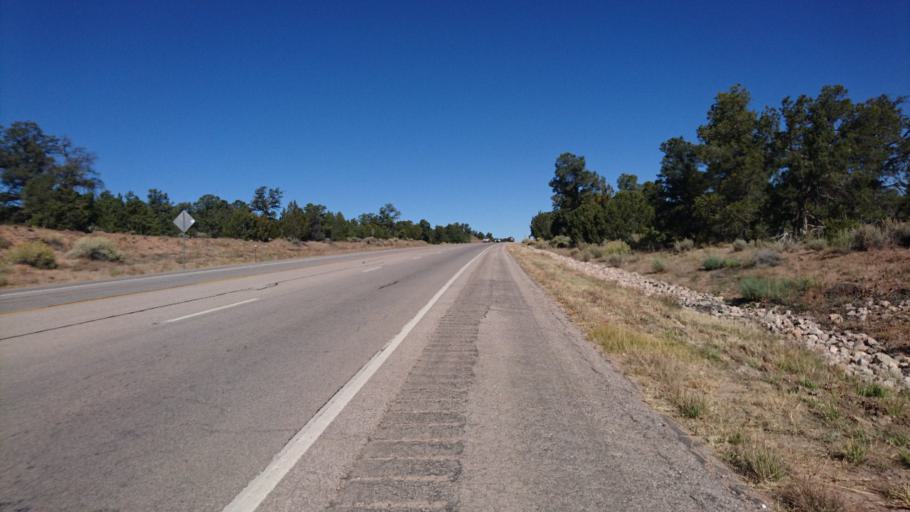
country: US
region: New Mexico
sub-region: McKinley County
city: Black Rock
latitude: 35.2240
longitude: -108.7661
